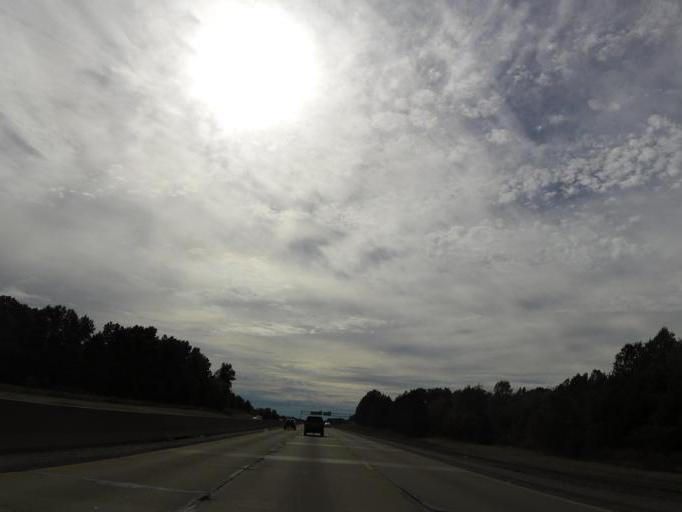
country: US
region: Ohio
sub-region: Summit County
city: Hudson
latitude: 41.2098
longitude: -81.4865
